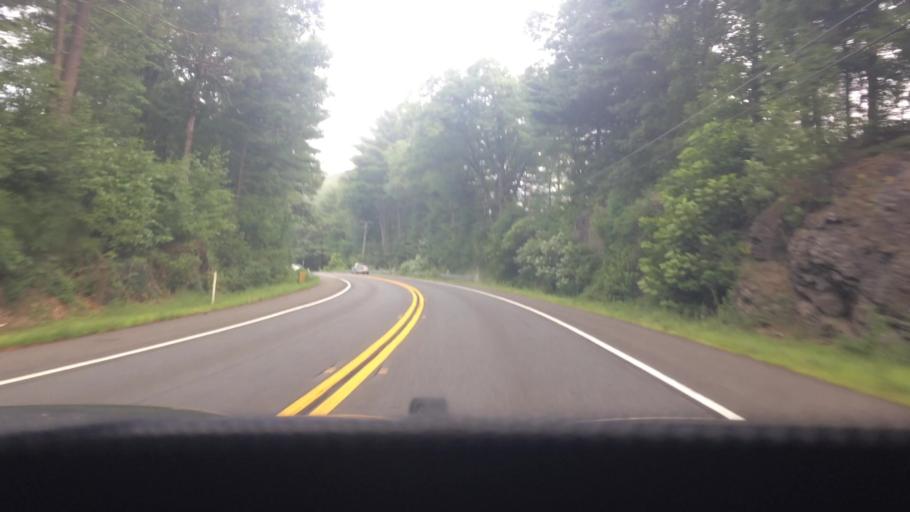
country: US
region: Massachusetts
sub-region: Franklin County
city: Millers Falls
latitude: 42.6077
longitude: -72.5052
